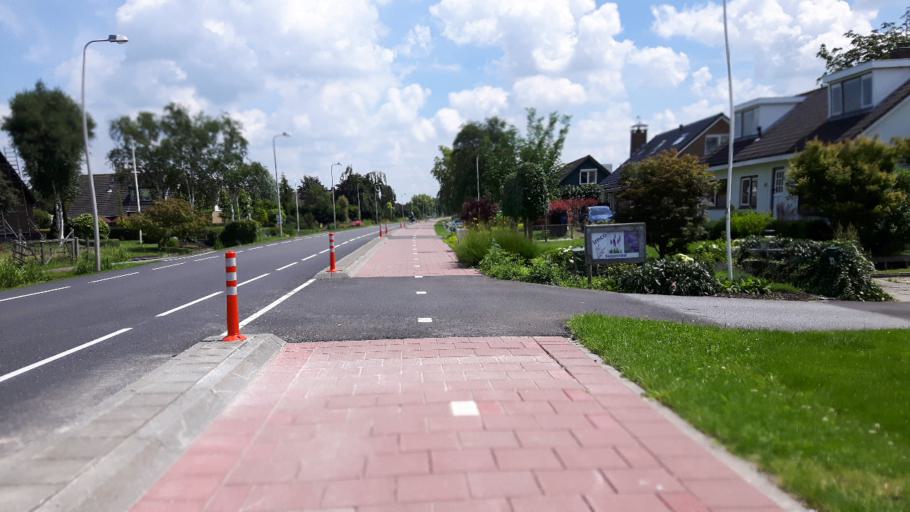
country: NL
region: South Holland
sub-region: Gemeente Boskoop
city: Boskoop
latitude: 52.0923
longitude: 4.6875
